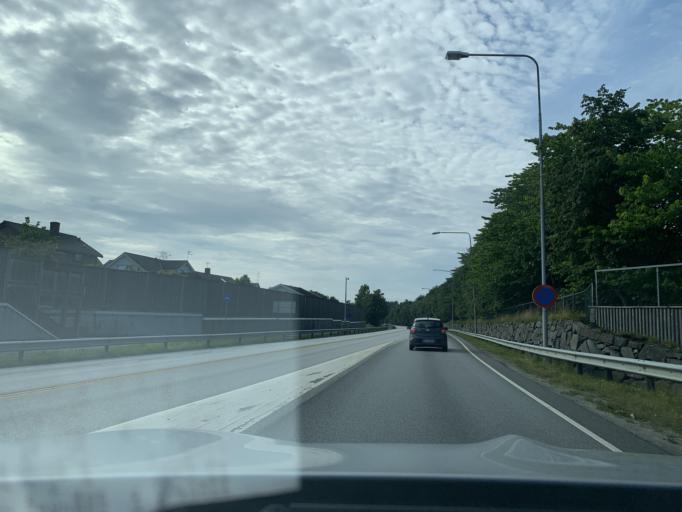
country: NO
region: Rogaland
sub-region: Stavanger
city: Stavanger
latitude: 58.9145
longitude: 5.7234
